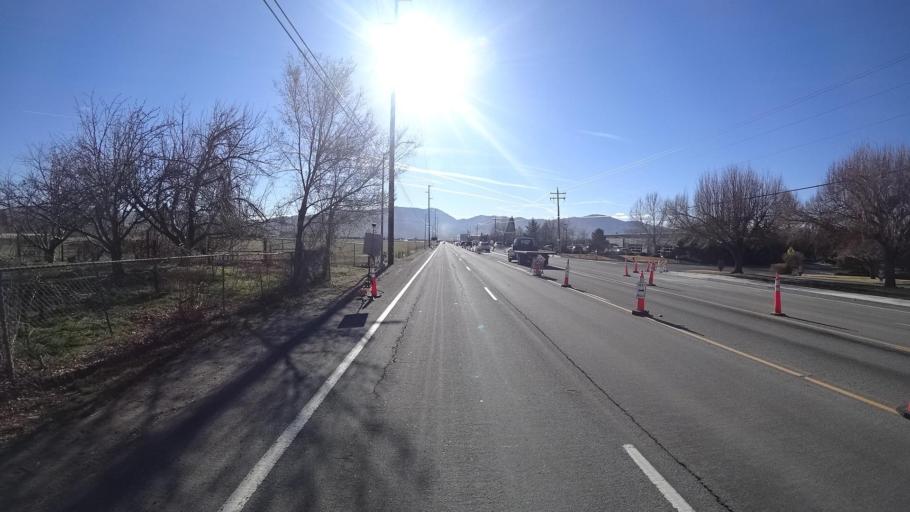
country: US
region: Nevada
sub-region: Washoe County
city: Sparks
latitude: 39.5134
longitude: -119.7493
